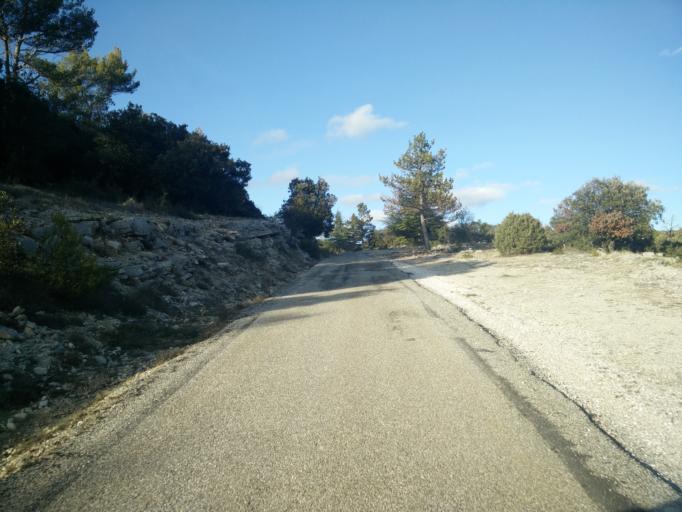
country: FR
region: Provence-Alpes-Cote d'Azur
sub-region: Departement du Var
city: Le Revest-les-Eaux
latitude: 43.2237
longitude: 5.9328
